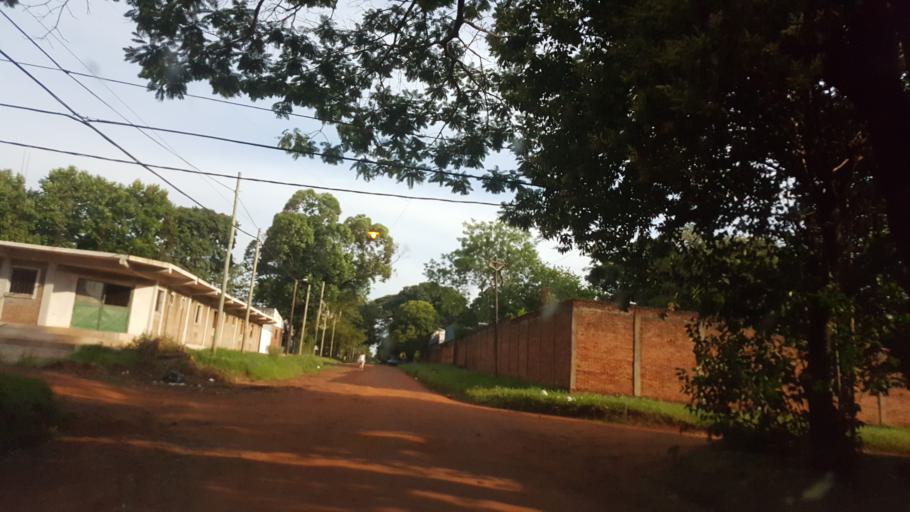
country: AR
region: Misiones
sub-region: Departamento de Capital
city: Posadas
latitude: -27.4294
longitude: -55.8875
